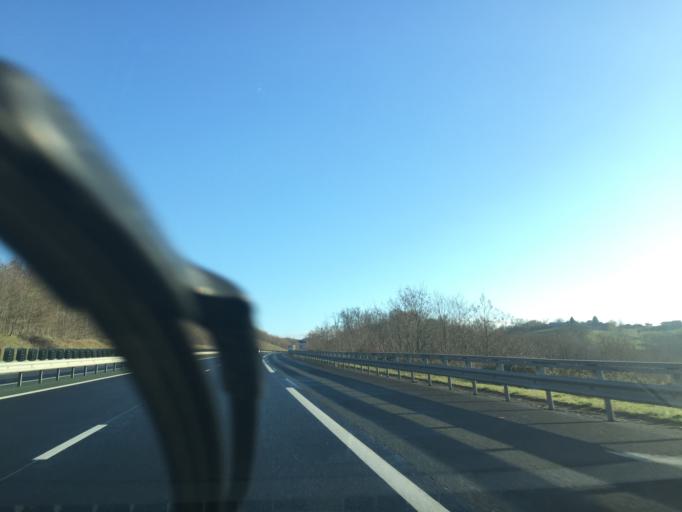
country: FR
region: Limousin
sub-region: Departement de la Correze
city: Mansac
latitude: 45.1634
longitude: 1.4032
